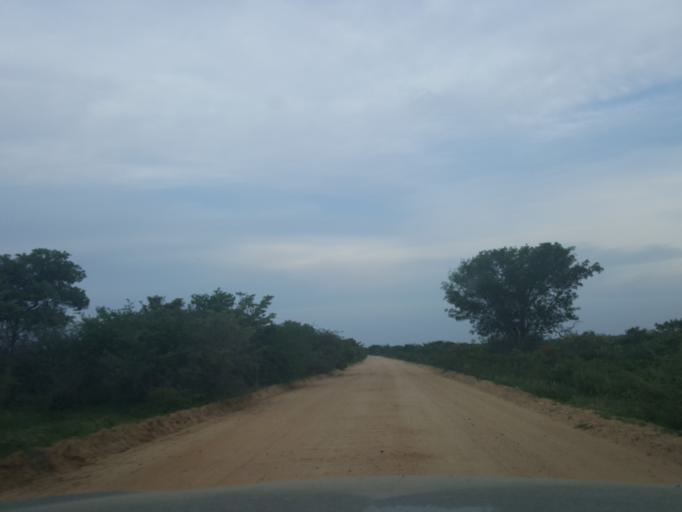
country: ZA
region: Limpopo
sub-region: Mopani District Municipality
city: Hoedspruit
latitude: -24.5668
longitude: 31.0080
